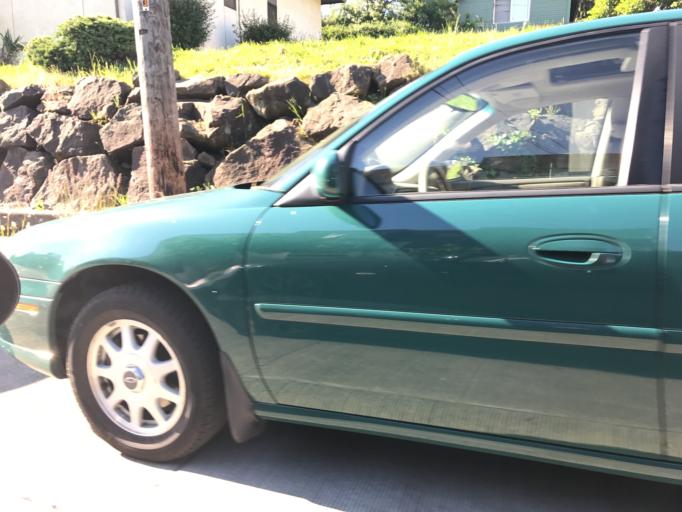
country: US
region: Washington
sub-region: King County
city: Seattle
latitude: 47.5884
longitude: -122.3090
